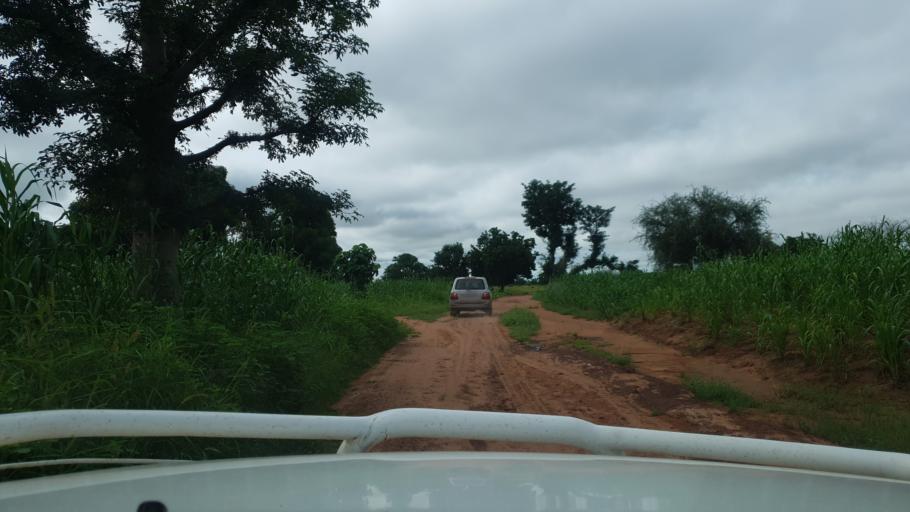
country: ML
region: Segou
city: Baroueli
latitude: 13.5014
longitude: -6.8980
